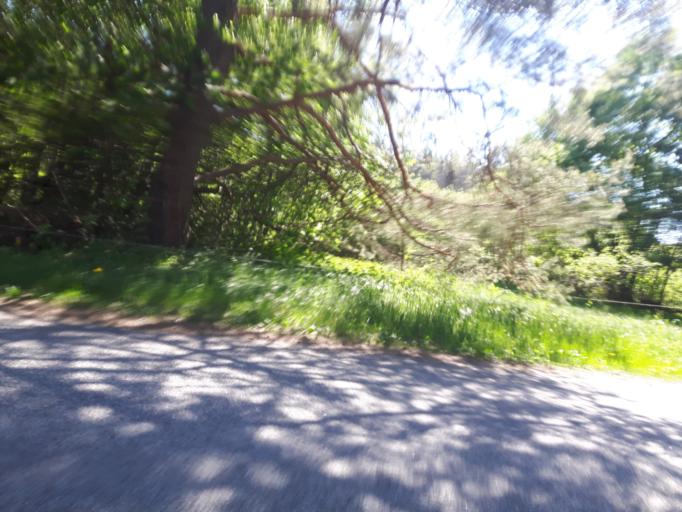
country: EE
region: Laeaene-Virumaa
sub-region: Viru-Nigula vald
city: Kunda
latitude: 59.5495
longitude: 26.3832
